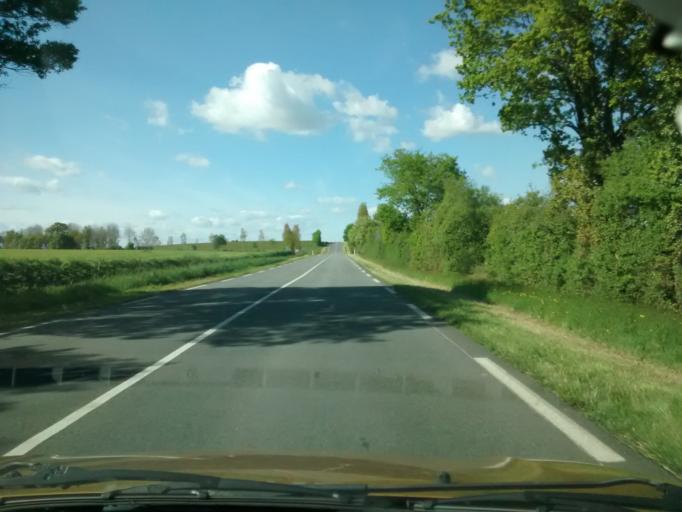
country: FR
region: Pays de la Loire
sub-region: Departement de la Vendee
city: Rocheserviere
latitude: 46.9036
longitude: -1.5030
